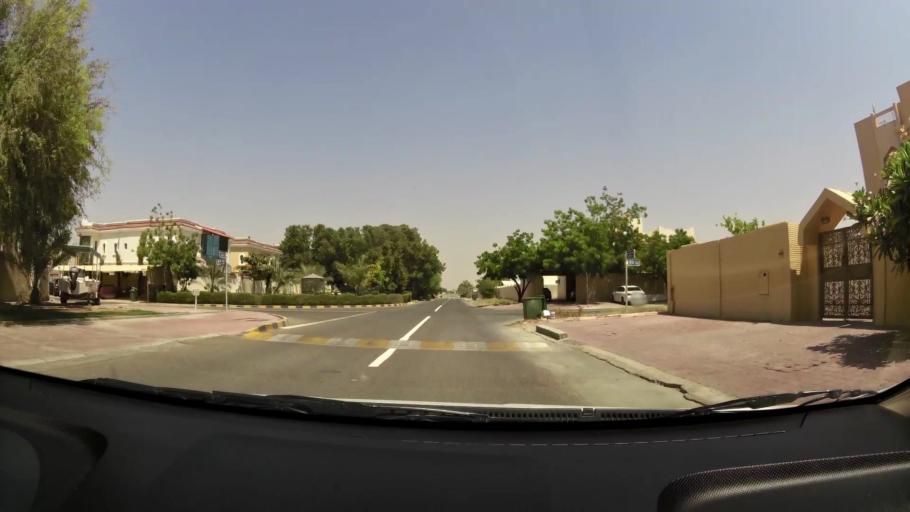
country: AE
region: Ajman
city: Ajman
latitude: 25.4276
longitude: 55.5073
